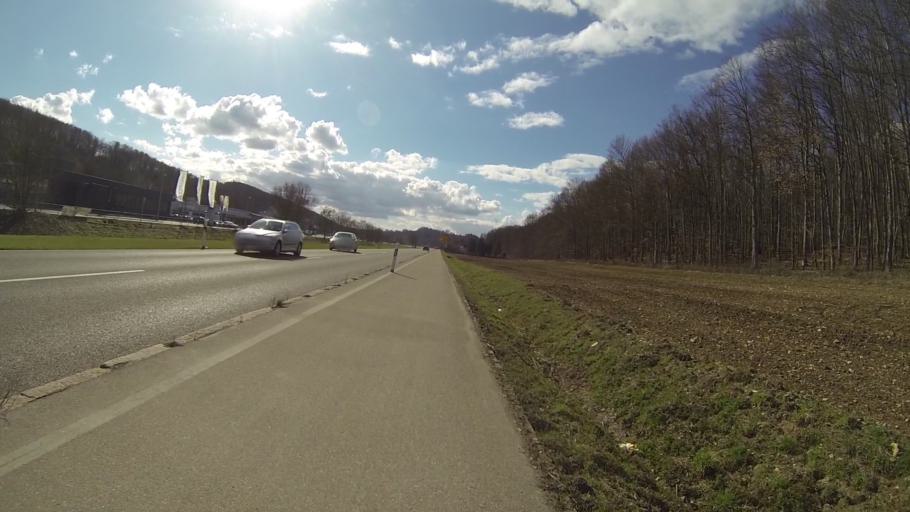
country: DE
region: Baden-Wuerttemberg
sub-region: Regierungsbezirk Stuttgart
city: Heidenheim an der Brenz
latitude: 48.6801
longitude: 10.1096
